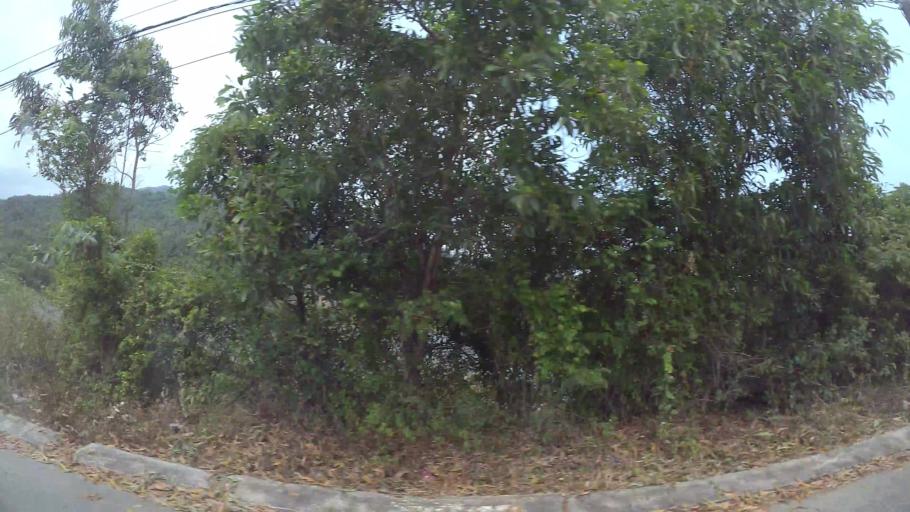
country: VN
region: Da Nang
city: Son Tra
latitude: 16.0984
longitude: 108.2669
